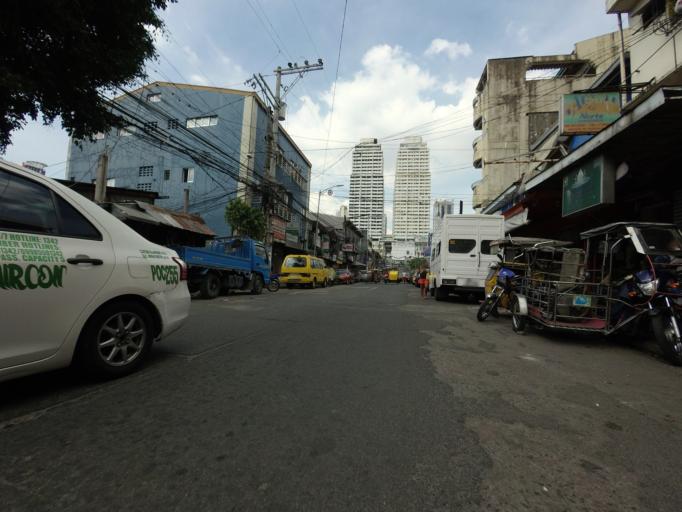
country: PH
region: Metro Manila
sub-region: City of Manila
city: Port Area
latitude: 14.5687
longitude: 120.9892
